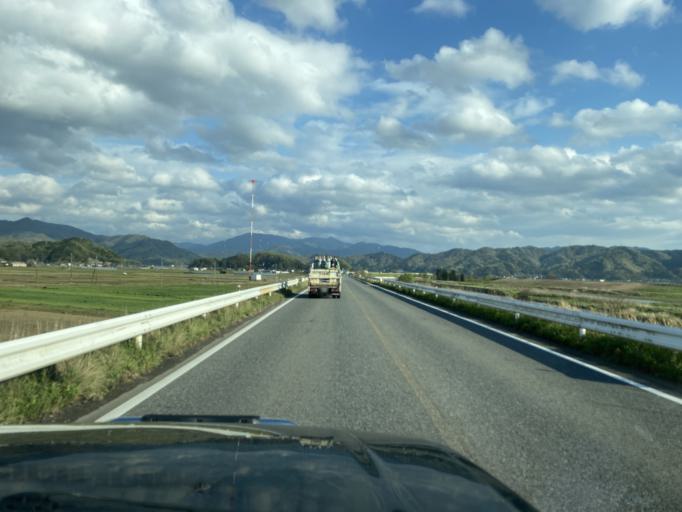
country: JP
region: Hyogo
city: Toyooka
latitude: 35.5051
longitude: 134.8355
